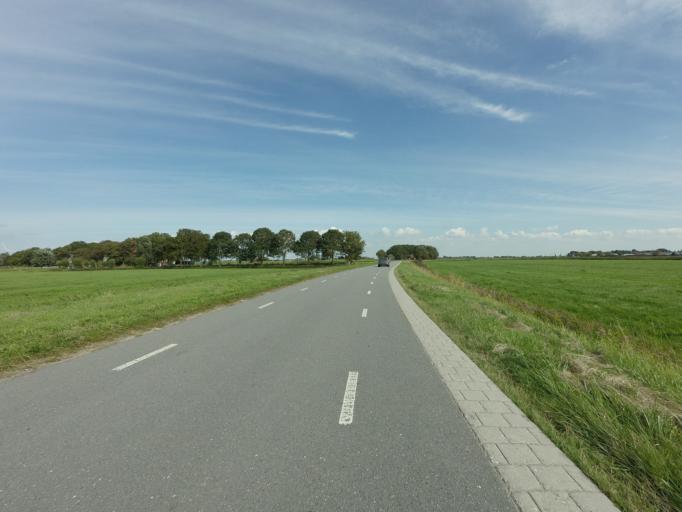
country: NL
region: Friesland
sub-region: Gemeente Harlingen
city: Harlingen
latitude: 53.1733
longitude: 5.4582
